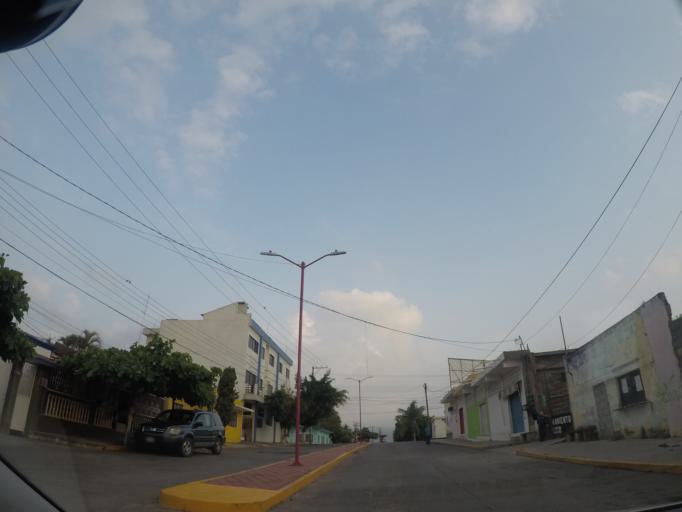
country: MX
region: Oaxaca
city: Matias Romero
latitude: 16.8756
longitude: -95.0409
